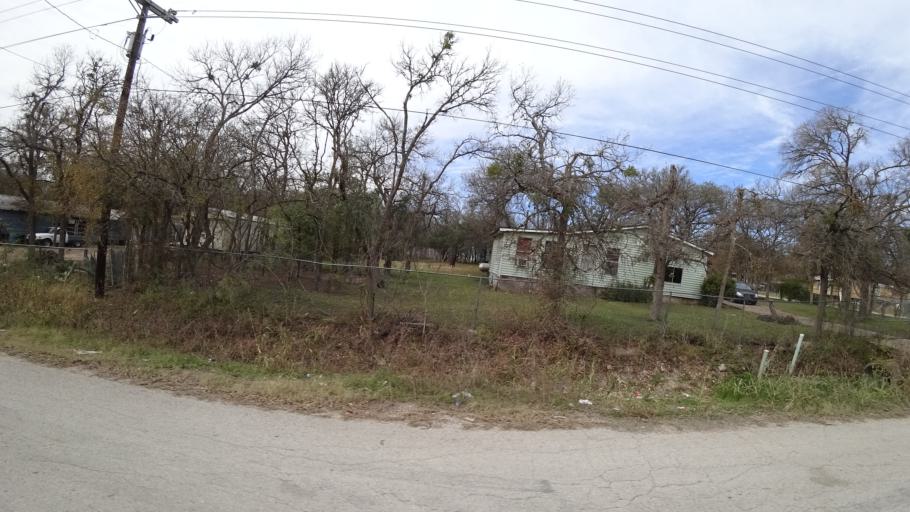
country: US
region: Texas
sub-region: Travis County
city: Garfield
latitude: 30.1325
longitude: -97.5651
